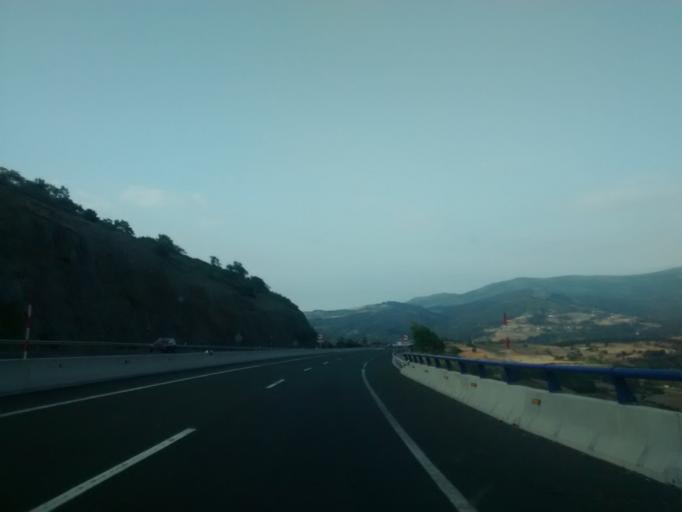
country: ES
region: Cantabria
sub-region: Provincia de Cantabria
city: Barcena de Pie de Concha
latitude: 43.1297
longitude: -4.0720
